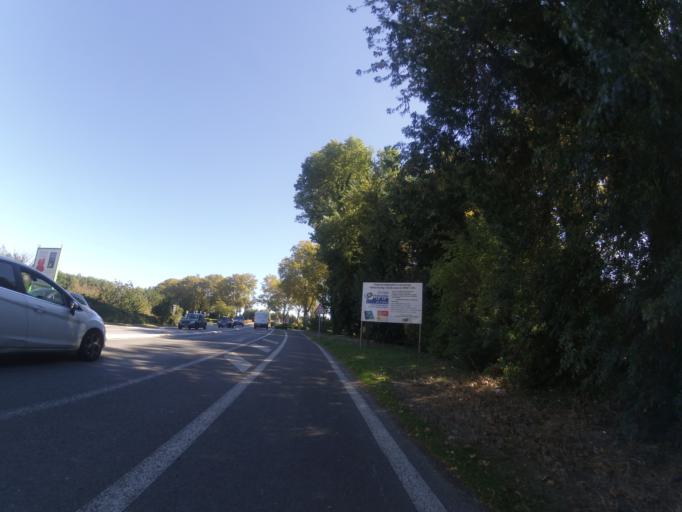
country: FR
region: Languedoc-Roussillon
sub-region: Departement des Pyrenees-Orientales
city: Saint-Esteve
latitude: 42.7095
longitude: 2.8628
